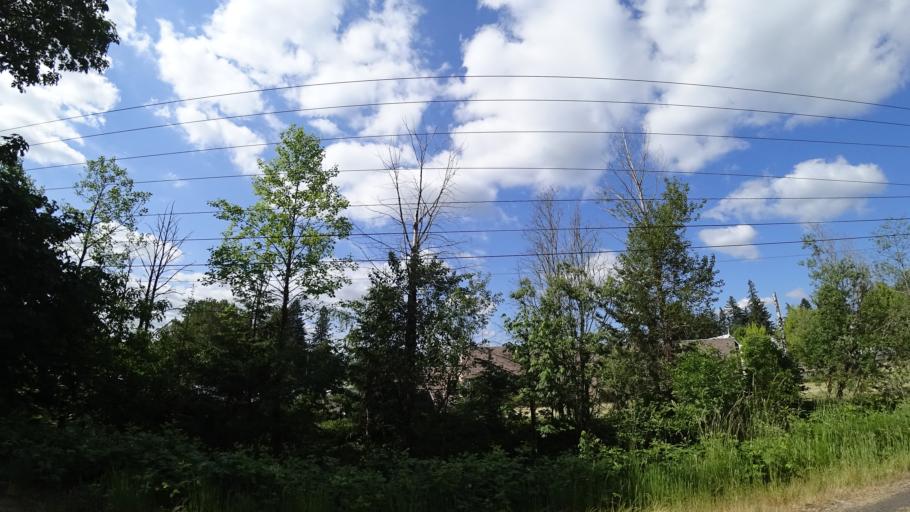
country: US
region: Oregon
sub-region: Washington County
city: Garden Home-Whitford
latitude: 45.4675
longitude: -122.7189
